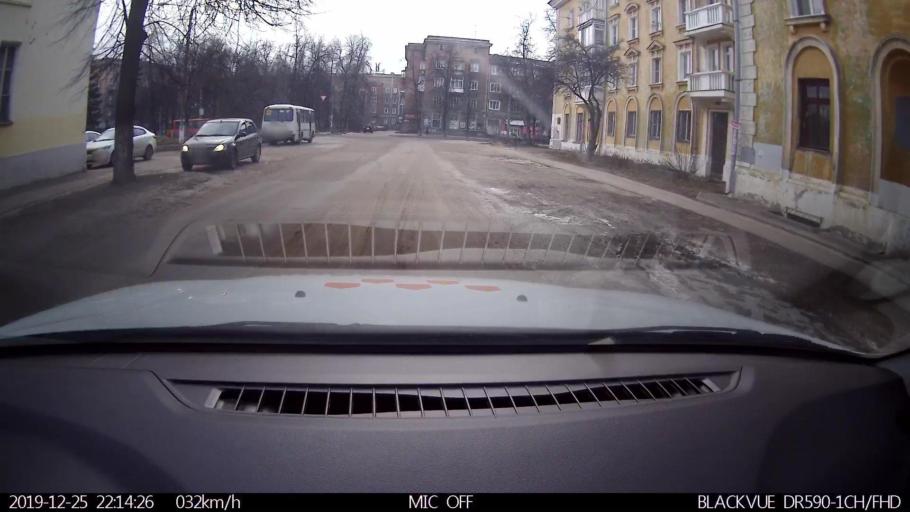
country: RU
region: Nizjnij Novgorod
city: Gorbatovka
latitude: 56.3311
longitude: 43.8455
